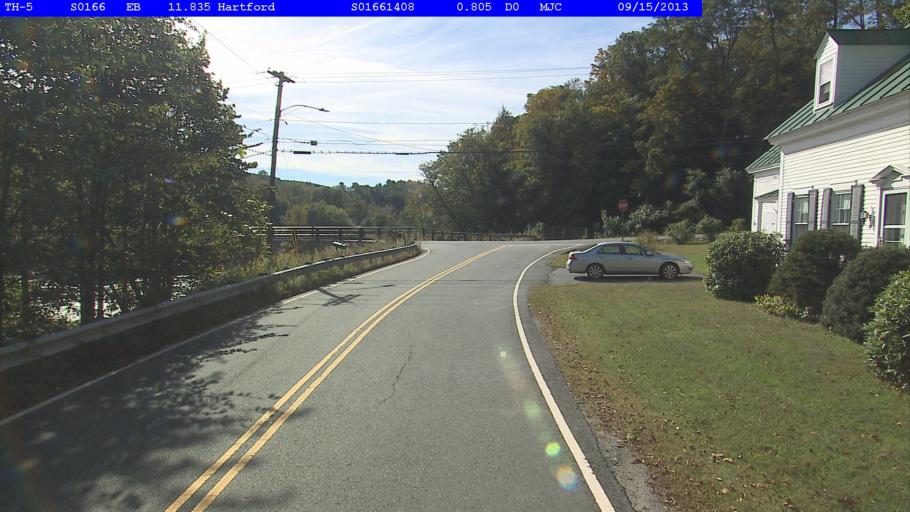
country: US
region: Vermont
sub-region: Windsor County
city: Wilder
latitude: 43.7124
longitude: -72.4188
